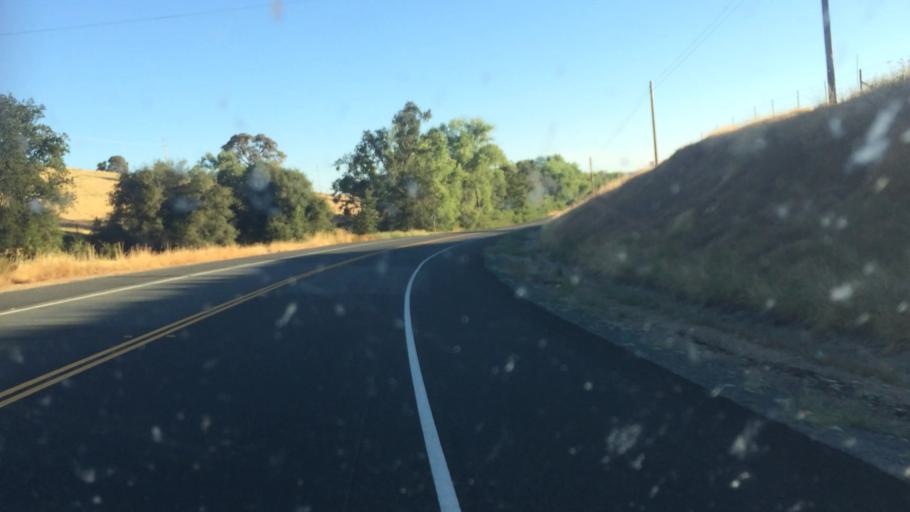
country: US
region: California
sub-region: El Dorado County
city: Deer Park
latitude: 38.6523
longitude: -120.8535
